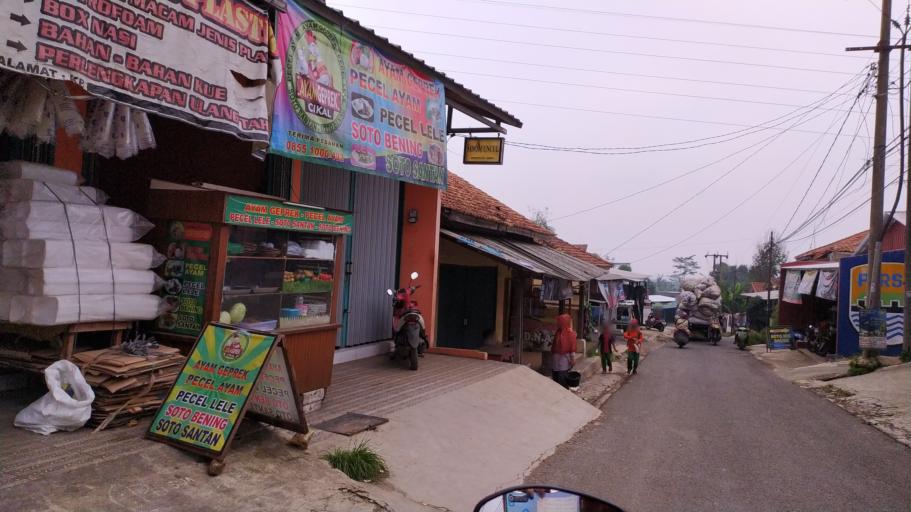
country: ID
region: West Java
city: Ciampea
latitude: -6.5907
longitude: 106.7038
